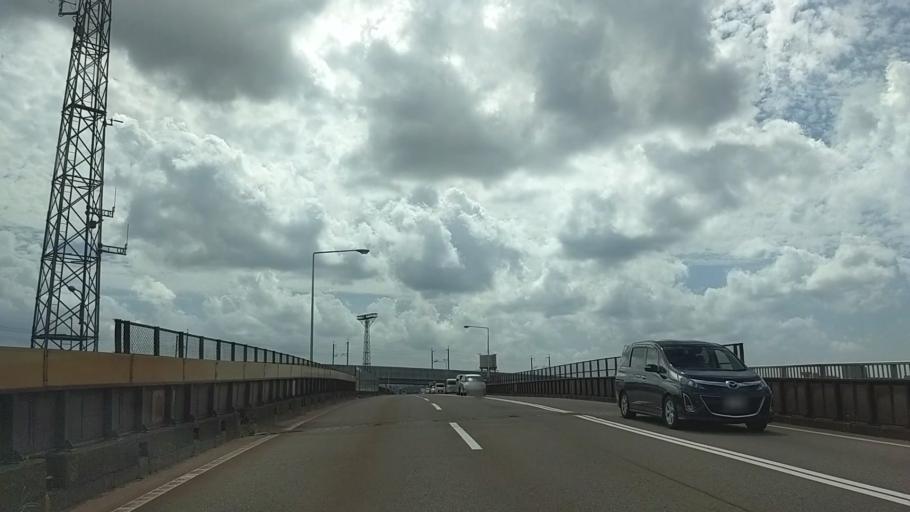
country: JP
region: Ishikawa
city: Kanazawa-shi
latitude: 36.5897
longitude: 136.6633
